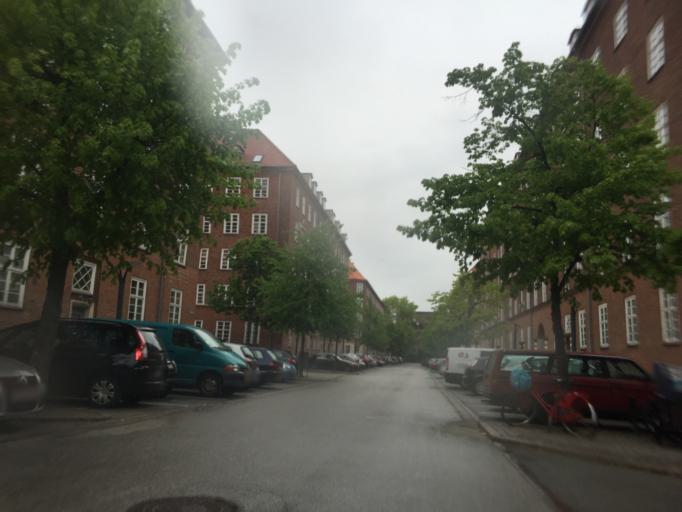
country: DK
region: Capital Region
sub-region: Frederiksberg Kommune
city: Frederiksberg
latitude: 55.6825
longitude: 12.5134
